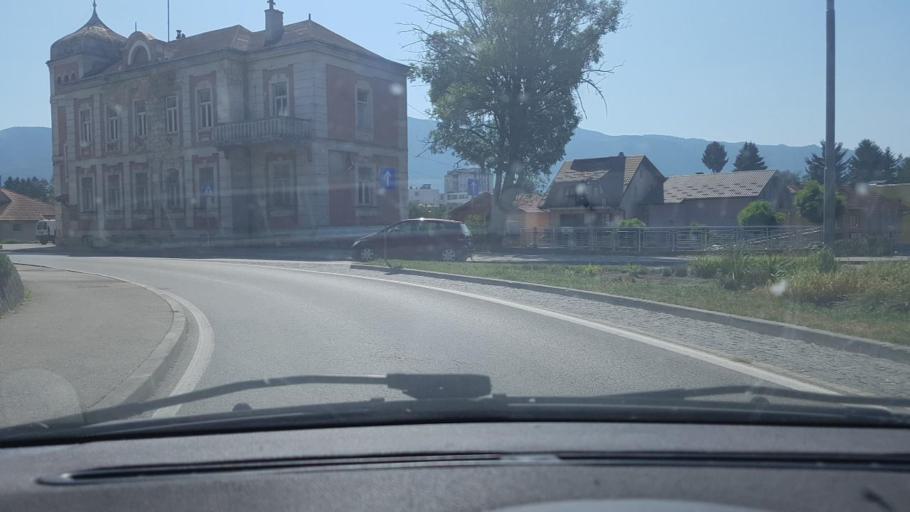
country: BA
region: Federation of Bosnia and Herzegovina
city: Bihac
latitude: 44.8170
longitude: 15.8689
